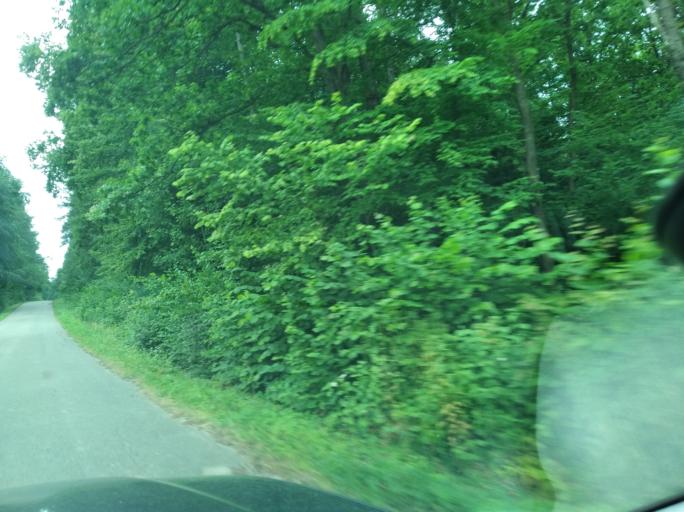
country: PL
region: Subcarpathian Voivodeship
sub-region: Powiat przeworski
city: Lopuszka Wielka
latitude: 49.9100
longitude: 22.3977
